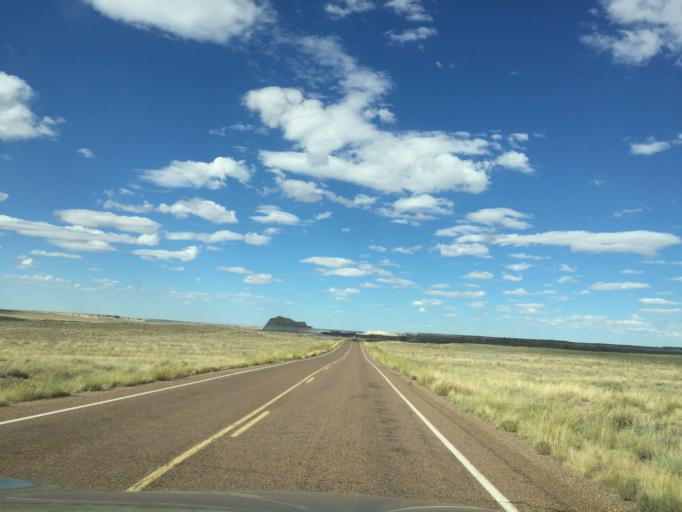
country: US
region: Arizona
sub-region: Navajo County
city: Holbrook
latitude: 34.8557
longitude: -109.7968
